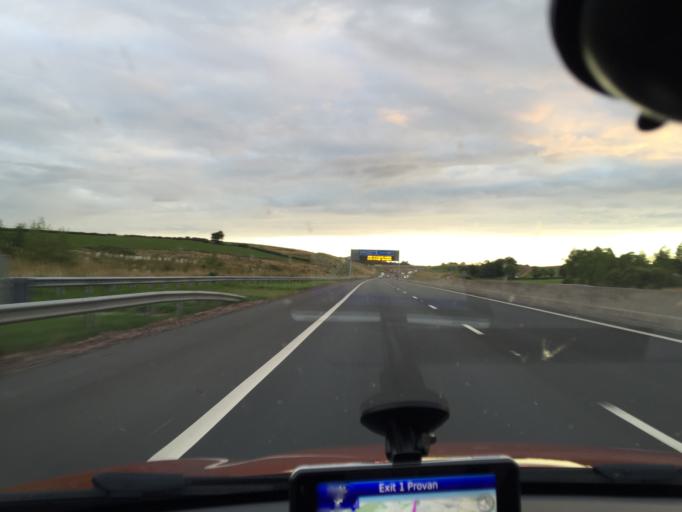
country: GB
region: Scotland
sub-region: North Lanarkshire
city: Chryston
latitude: 55.9156
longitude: -4.1092
